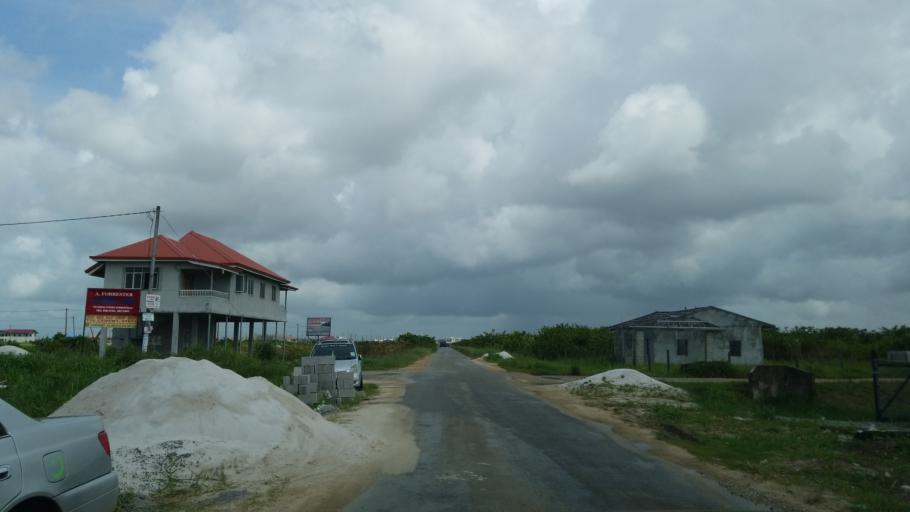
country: GY
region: Demerara-Mahaica
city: Georgetown
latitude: 6.7551
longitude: -58.1536
